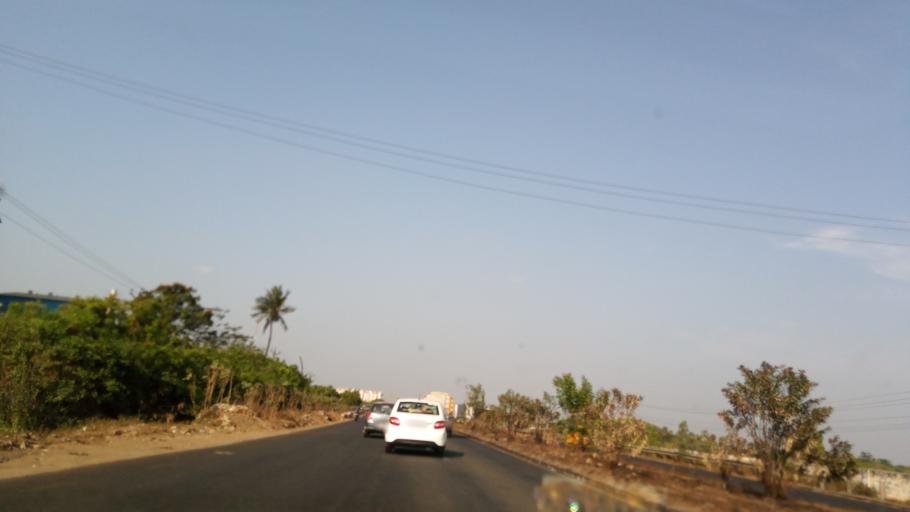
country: IN
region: Tamil Nadu
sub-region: Kancheepuram
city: Nandambakkam
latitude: 13.0172
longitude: 80.0082
